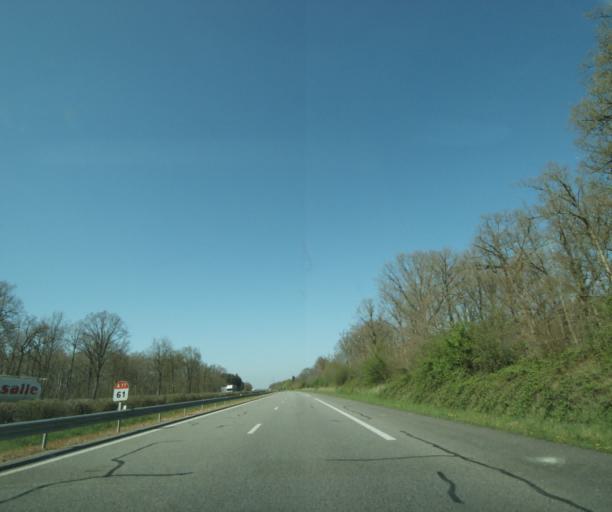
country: FR
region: Centre
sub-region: Departement du Loiret
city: Ouzouer-sur-Trezee
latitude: 47.7115
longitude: 2.7410
